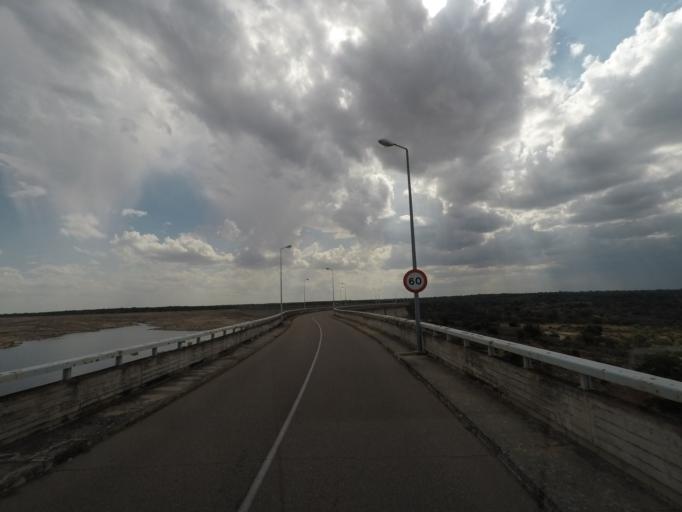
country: ES
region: Castille and Leon
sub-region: Provincia de Salamanca
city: Almendra
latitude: 41.2678
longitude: -6.3214
